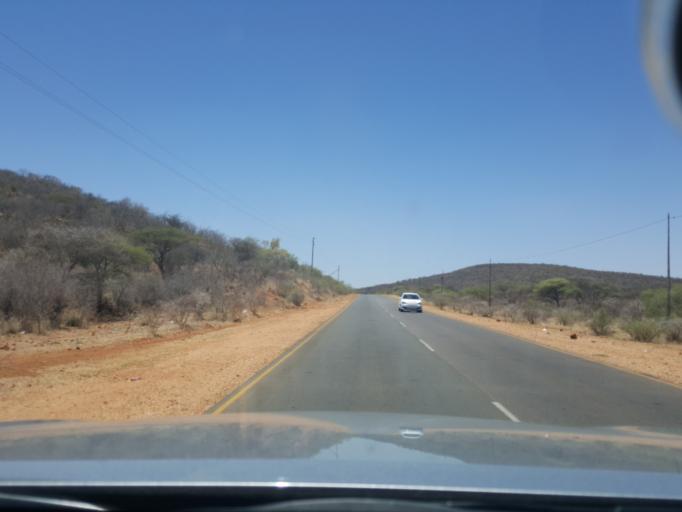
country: ZA
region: North-West
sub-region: Ngaka Modiri Molema District Municipality
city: Zeerust
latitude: -25.3785
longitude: 25.9351
